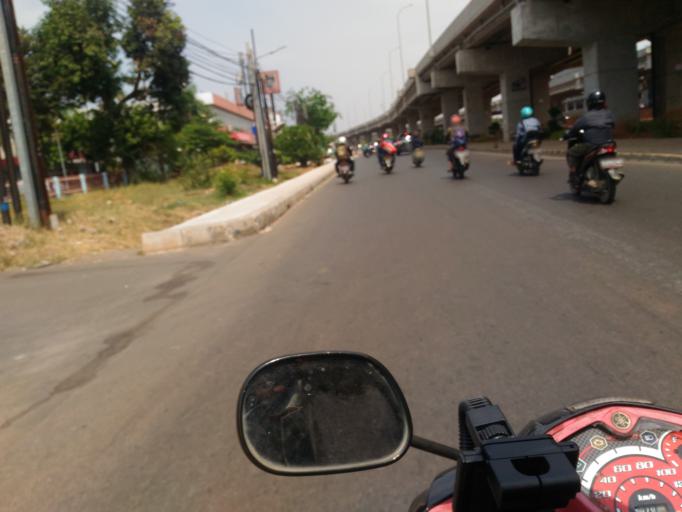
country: ID
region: Jakarta Raya
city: Jakarta
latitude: -6.2476
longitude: 106.9112
